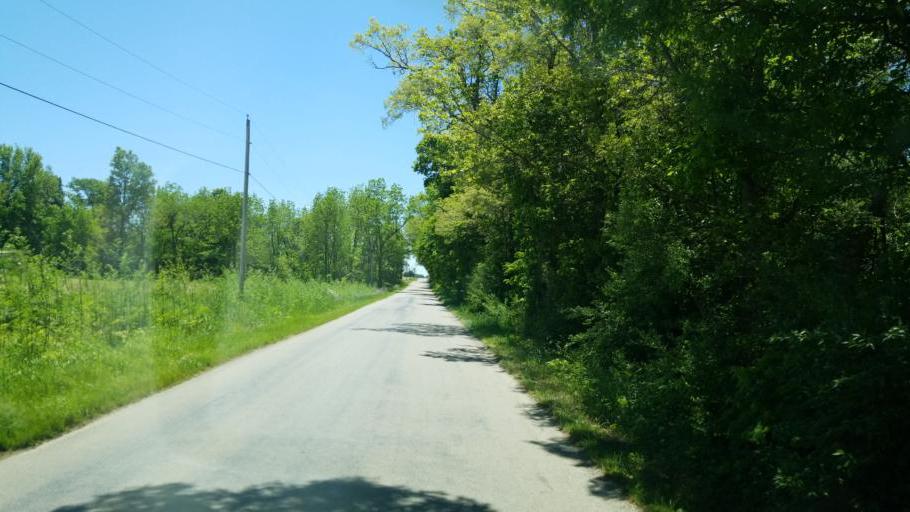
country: US
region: Ohio
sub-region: Mercer County
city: Fort Recovery
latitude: 40.3502
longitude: -84.8039
